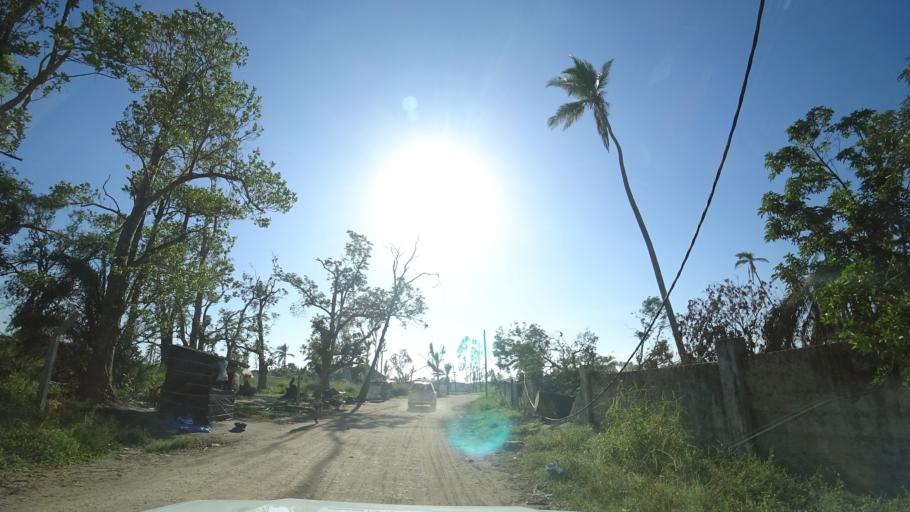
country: MZ
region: Sofala
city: Beira
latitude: -19.7649
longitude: 34.8969
